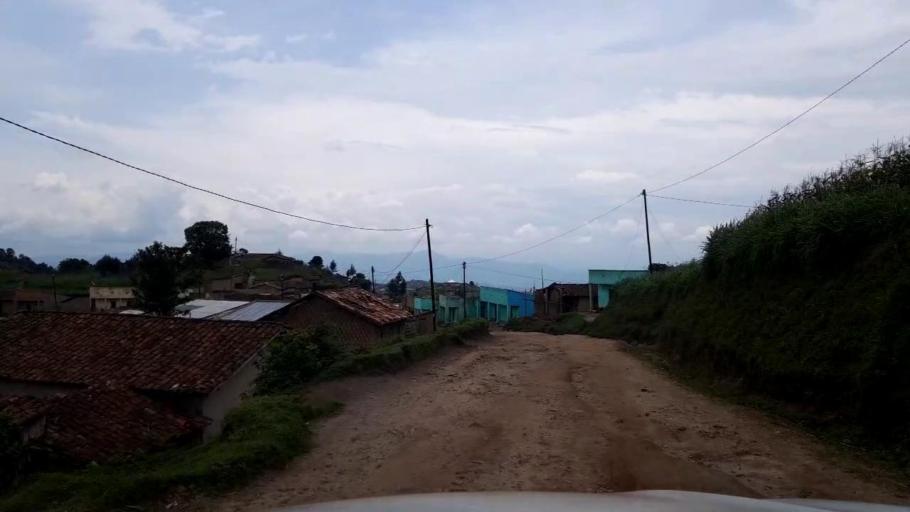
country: RW
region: Western Province
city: Kibuye
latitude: -1.9564
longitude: 29.4219
